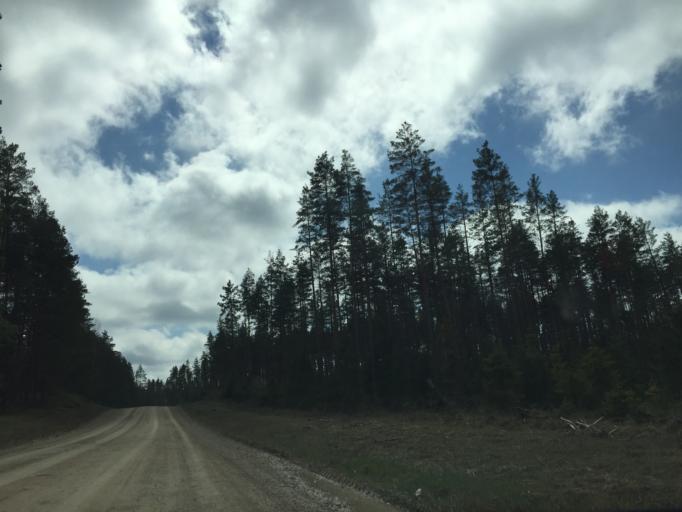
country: EE
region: Valgamaa
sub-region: Valga linn
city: Valga
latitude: 57.6406
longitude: 26.2313
